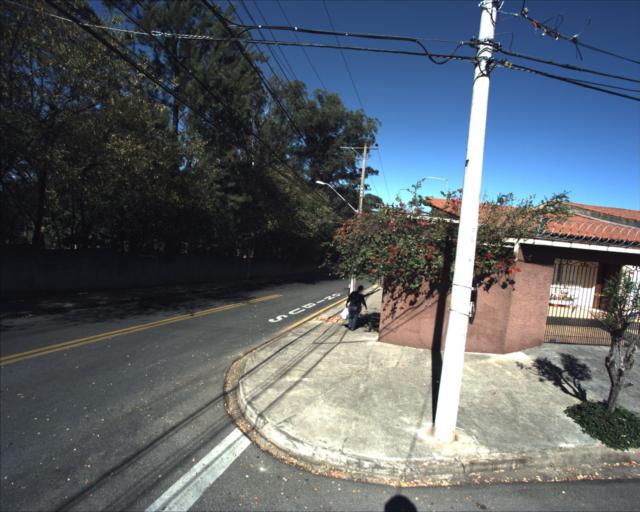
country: BR
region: Sao Paulo
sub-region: Sorocaba
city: Sorocaba
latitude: -23.4806
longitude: -47.4327
